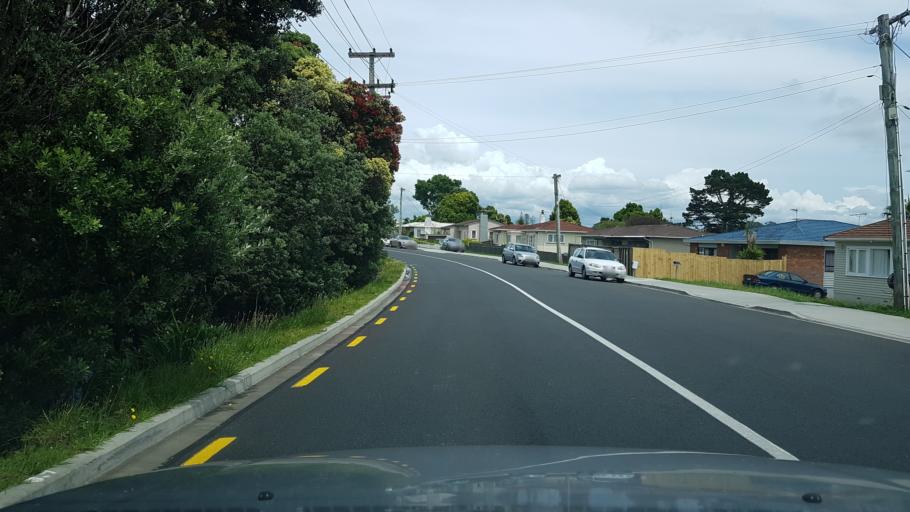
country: NZ
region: Auckland
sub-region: Auckland
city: North Shore
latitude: -36.7989
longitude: 174.7505
